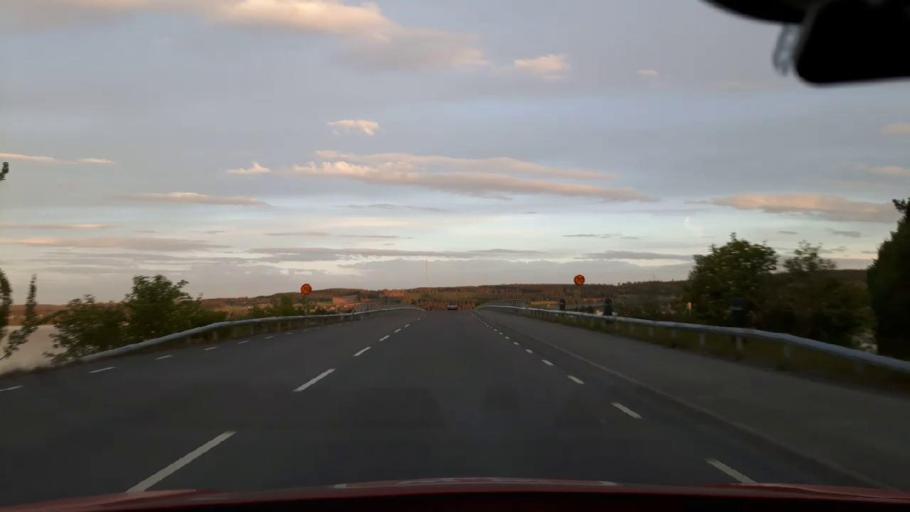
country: SE
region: Jaemtland
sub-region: OEstersunds Kommun
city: Ostersund
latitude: 63.1679
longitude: 14.6088
